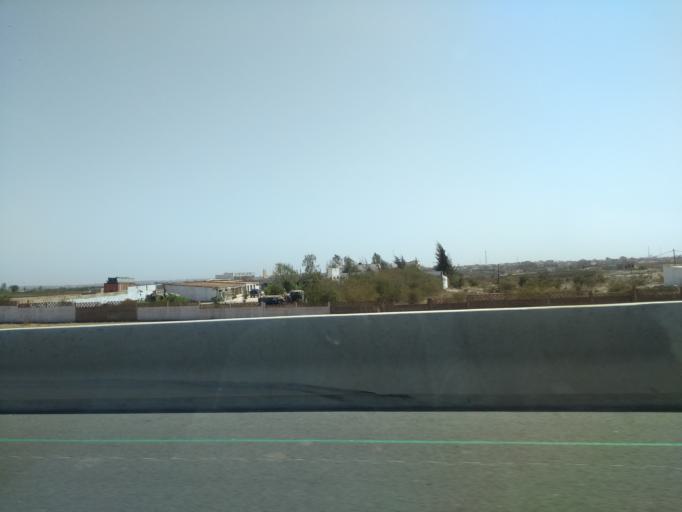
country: SN
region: Thies
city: Pout
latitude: 14.7355
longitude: -17.1774
